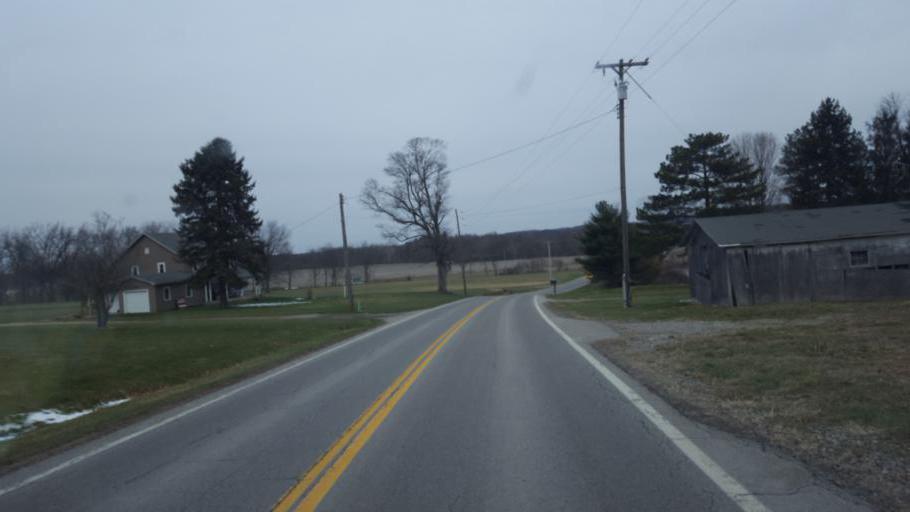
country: US
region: Ohio
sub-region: Richland County
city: Lexington
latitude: 40.6131
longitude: -82.5897
